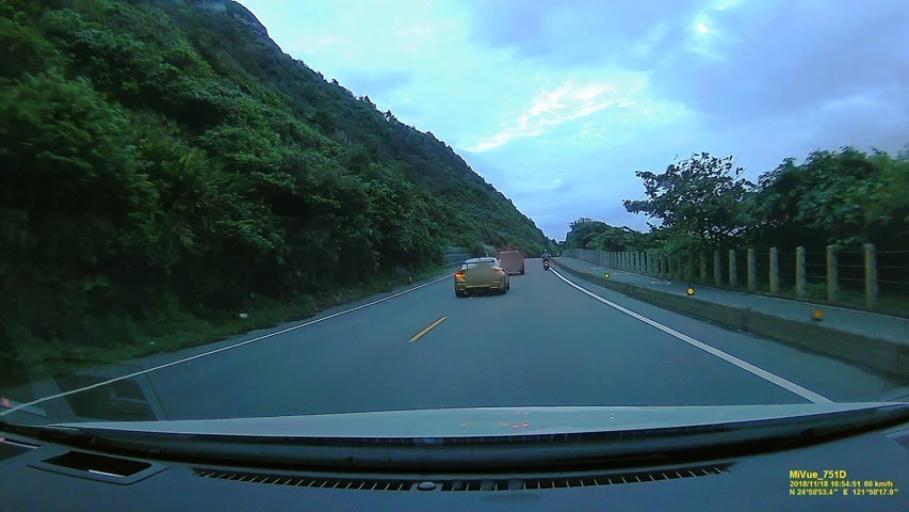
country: TW
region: Taiwan
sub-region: Keelung
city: Keelung
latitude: 24.9979
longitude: 121.9879
